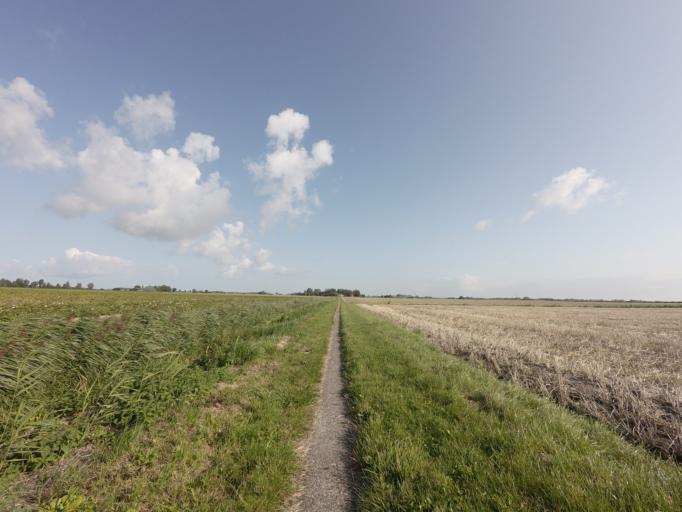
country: NL
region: Friesland
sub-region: Gemeente Franekeradeel
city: Franeker
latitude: 53.2046
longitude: 5.5645
